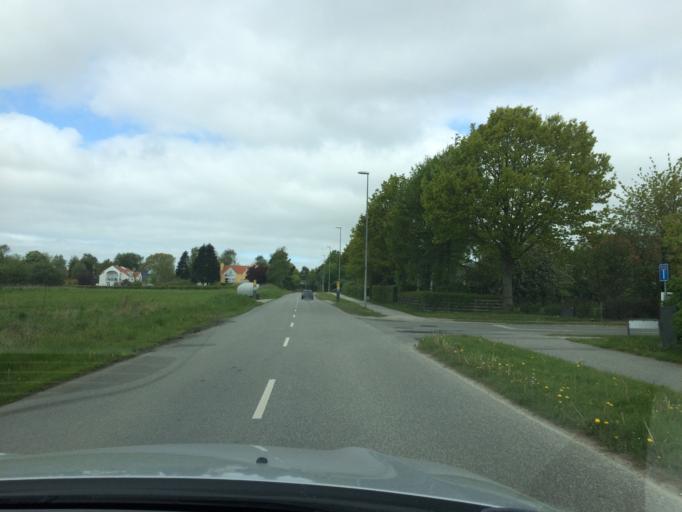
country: DK
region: Central Jutland
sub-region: Arhus Kommune
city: Hjortshoj
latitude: 56.2291
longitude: 10.3033
